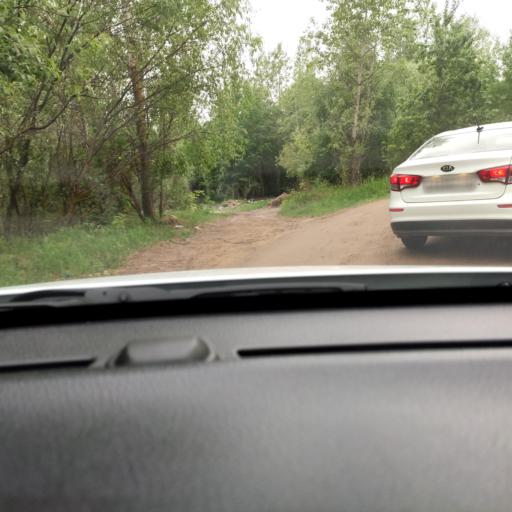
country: RU
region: Tatarstan
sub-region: Gorod Kazan'
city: Kazan
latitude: 55.8457
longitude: 49.1807
